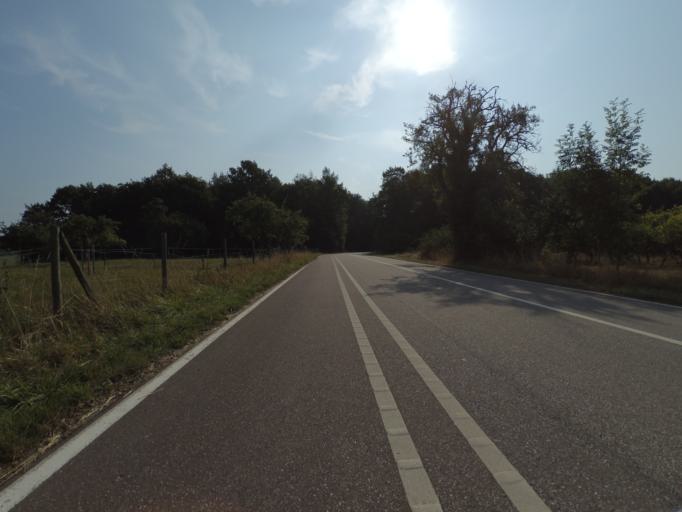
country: LU
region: Grevenmacher
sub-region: Canton de Remich
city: Remich
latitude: 49.5187
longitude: 6.4006
